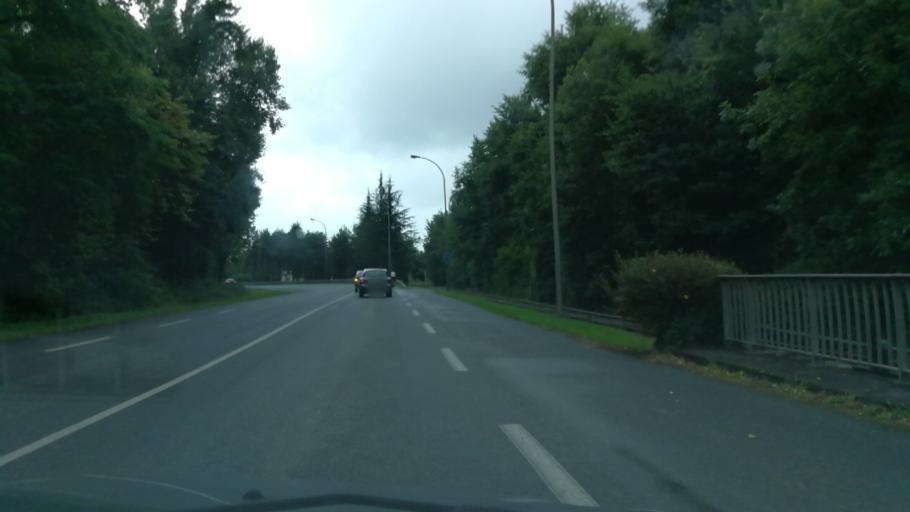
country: FR
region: Aquitaine
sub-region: Departement des Pyrenees-Atlantiques
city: Mourenx
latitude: 43.3897
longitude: -0.5806
